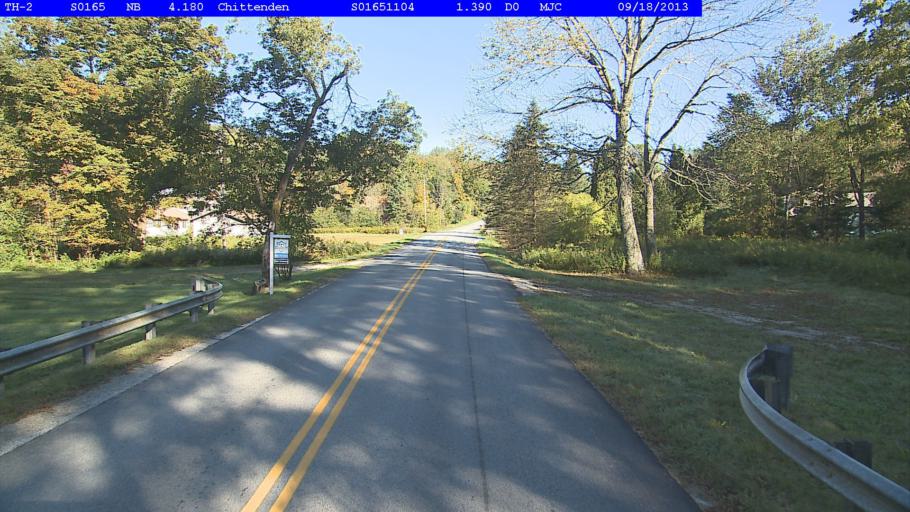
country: US
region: Vermont
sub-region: Rutland County
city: Rutland
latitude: 43.6960
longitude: -72.9568
